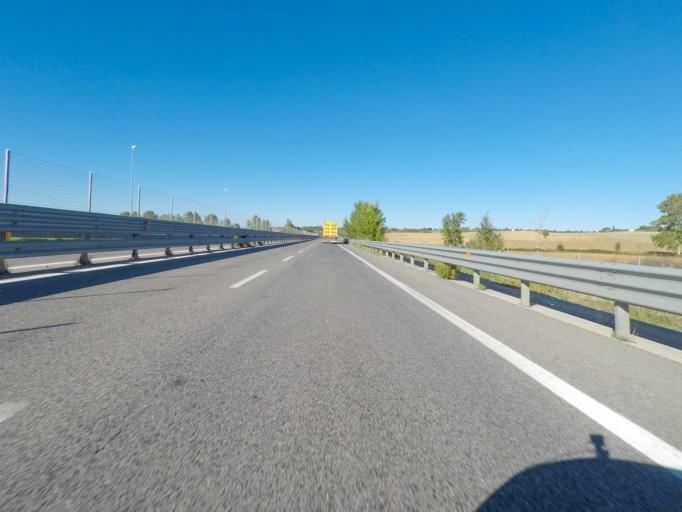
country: IT
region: Tuscany
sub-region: Provincia di Siena
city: Rosia
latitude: 43.2314
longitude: 11.2764
